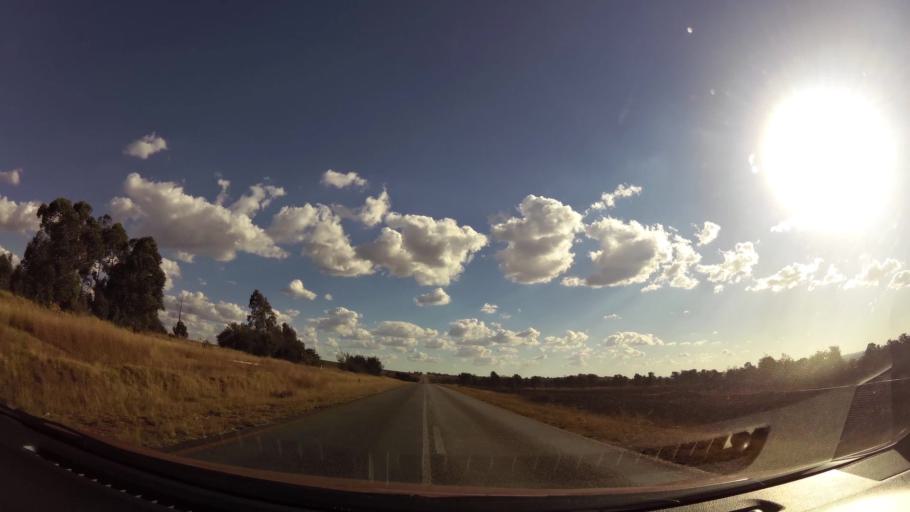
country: ZA
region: Gauteng
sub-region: West Rand District Municipality
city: Carletonville
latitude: -26.3832
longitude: 27.3665
